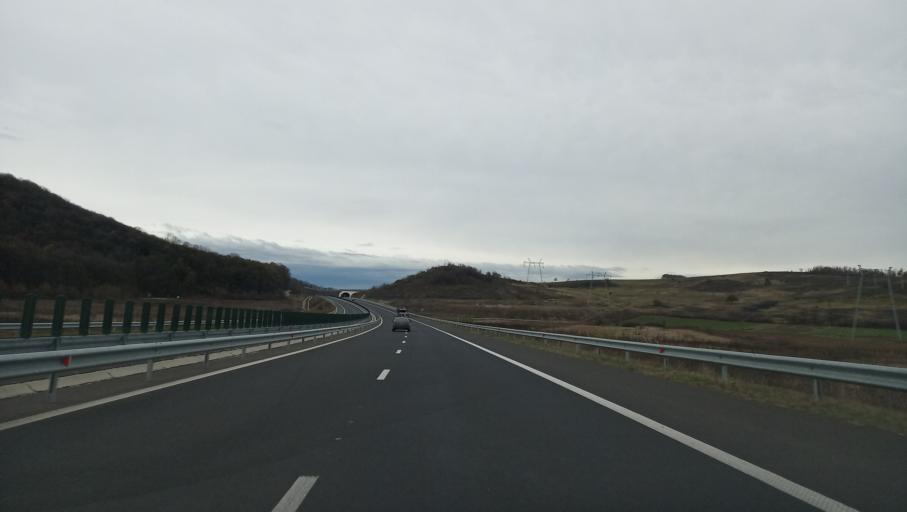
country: RO
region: Hunedoara
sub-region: Comuna Branisca
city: Branisca
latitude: 45.9366
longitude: 22.7511
